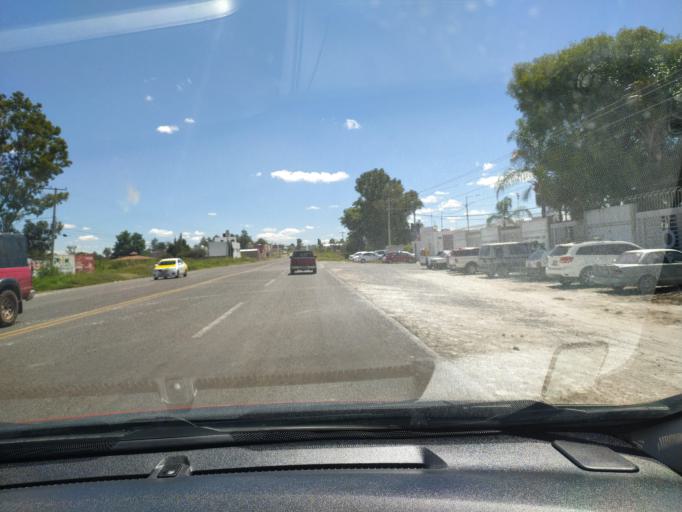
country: MX
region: Jalisco
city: San Miguel el Alto
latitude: 21.0273
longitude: -102.3796
